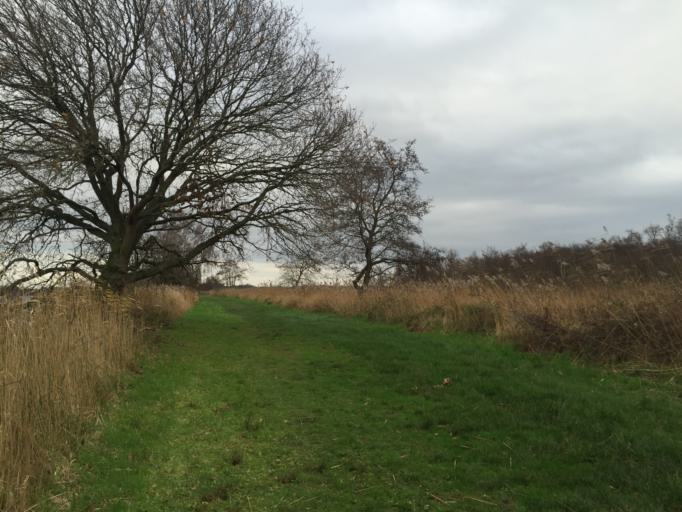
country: NL
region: North Holland
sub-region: Gemeente Wijdemeren
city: Kortenhoef
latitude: 52.2744
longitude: 5.0766
